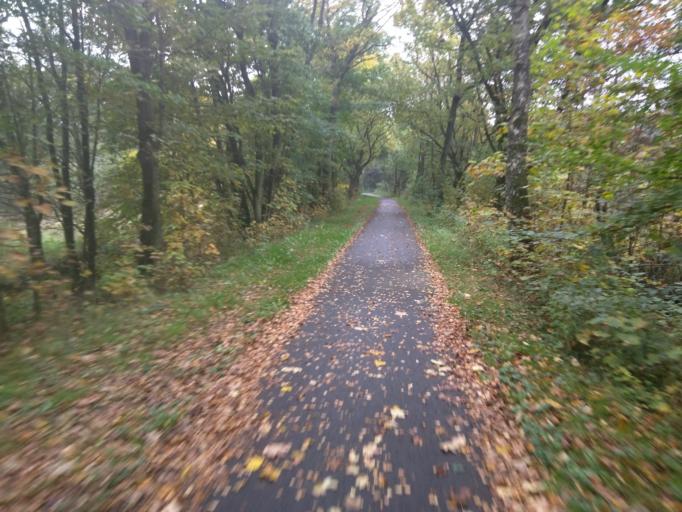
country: DK
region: Central Jutland
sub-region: Silkeborg Kommune
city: Silkeborg
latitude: 56.2406
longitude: 9.5299
